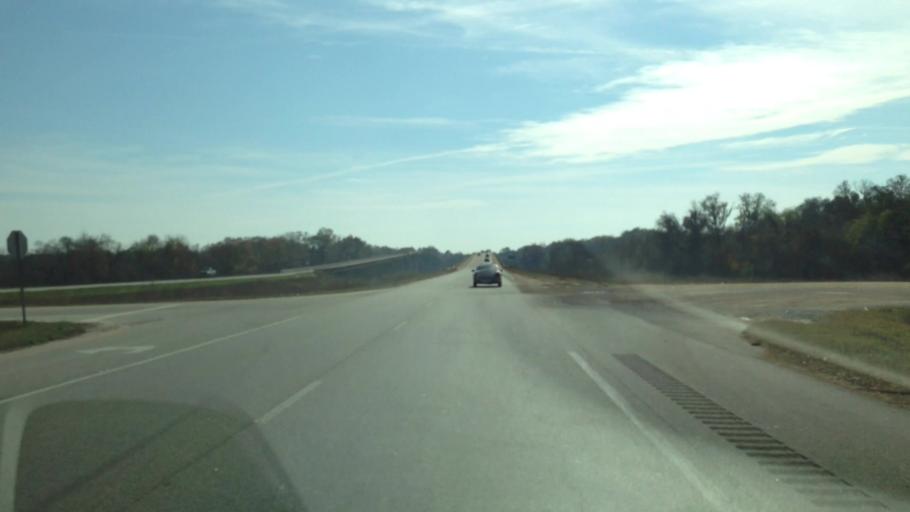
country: US
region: Alabama
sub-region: Autauga County
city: Prattville
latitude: 32.4175
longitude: -86.4104
